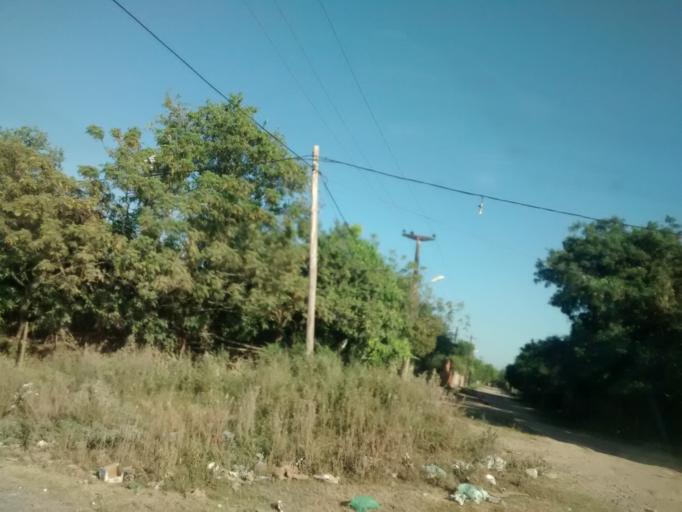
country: AR
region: Chaco
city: Resistencia
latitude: -27.4549
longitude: -58.9640
